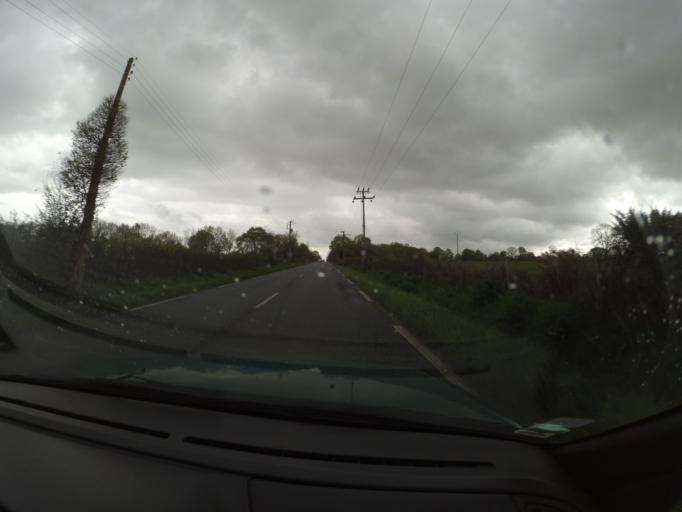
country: FR
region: Pays de la Loire
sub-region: Departement de la Loire-Atlantique
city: Vallet
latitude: 47.1877
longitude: -1.2542
